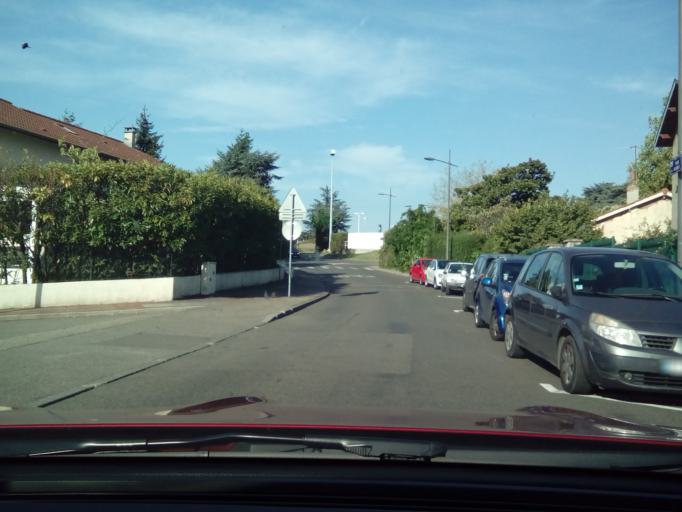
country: FR
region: Rhone-Alpes
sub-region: Departement du Rhone
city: Bron
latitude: 45.7390
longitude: 4.9063
